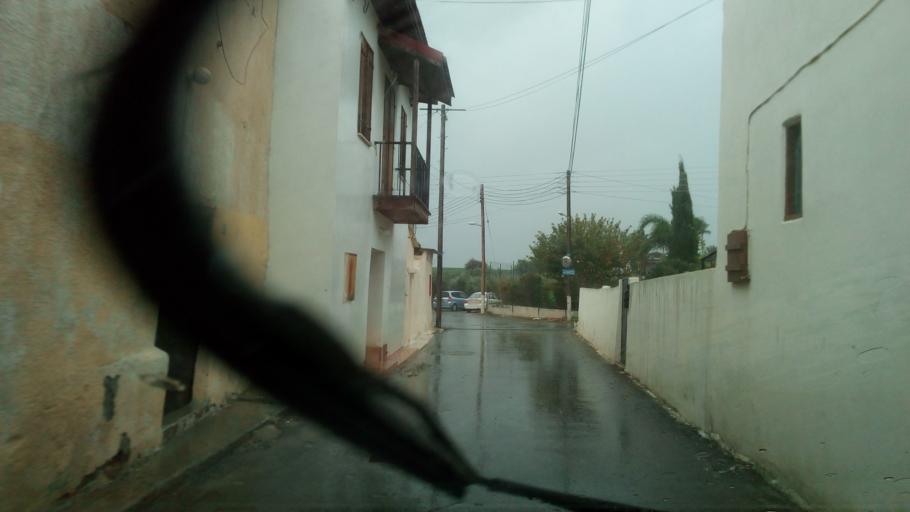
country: CY
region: Larnaka
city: Kofinou
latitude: 34.8475
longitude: 33.4619
